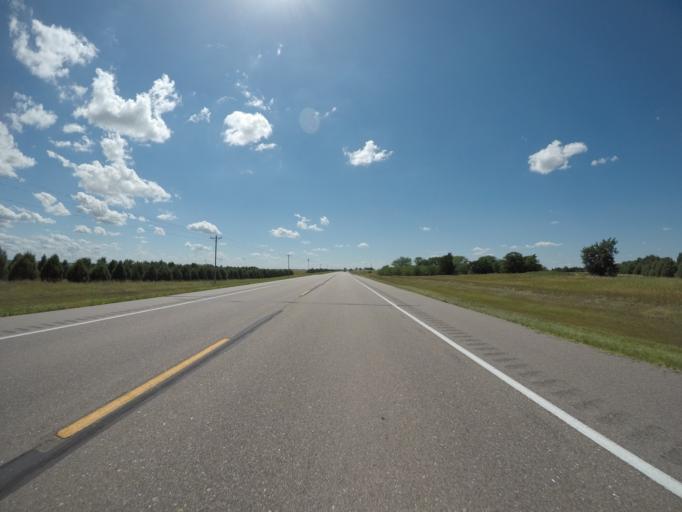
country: US
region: Nebraska
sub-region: Chase County
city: Imperial
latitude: 40.4947
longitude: -101.5690
